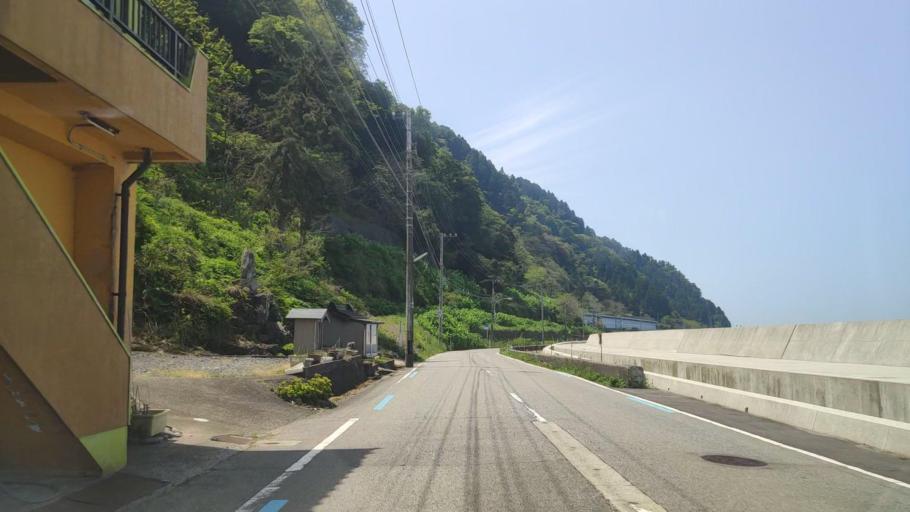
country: JP
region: Toyama
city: Nyuzen
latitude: 36.9719
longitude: 137.5860
